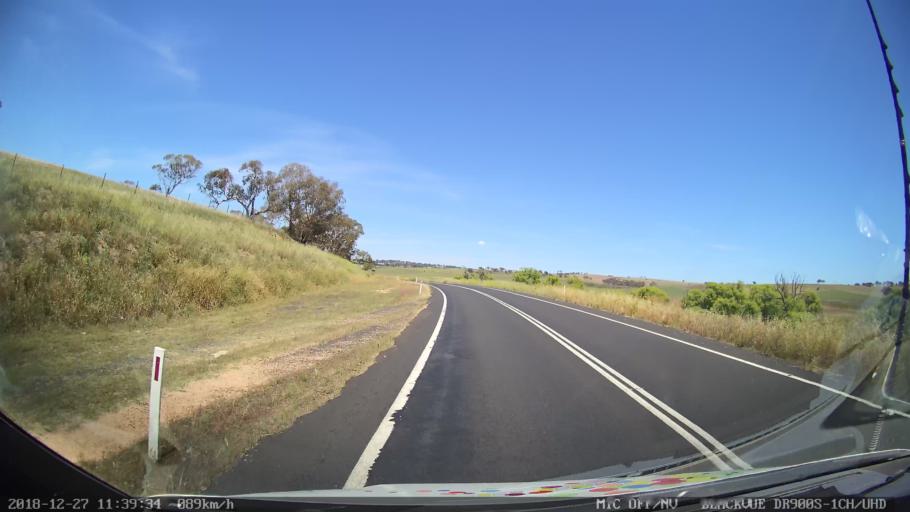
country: AU
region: New South Wales
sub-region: Bathurst Regional
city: Perthville
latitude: -33.5146
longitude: 149.4982
